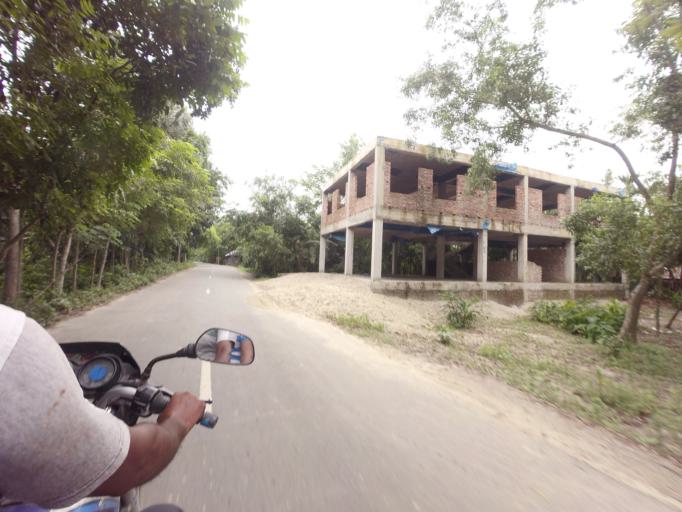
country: BD
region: Khulna
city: Kalia
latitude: 23.1543
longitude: 89.6447
